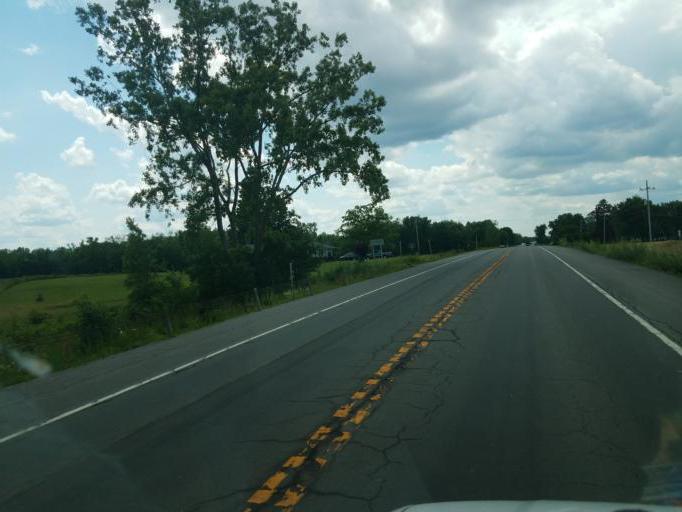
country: US
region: New York
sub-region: Seneca County
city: Waterloo
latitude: 42.9608
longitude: -76.8508
